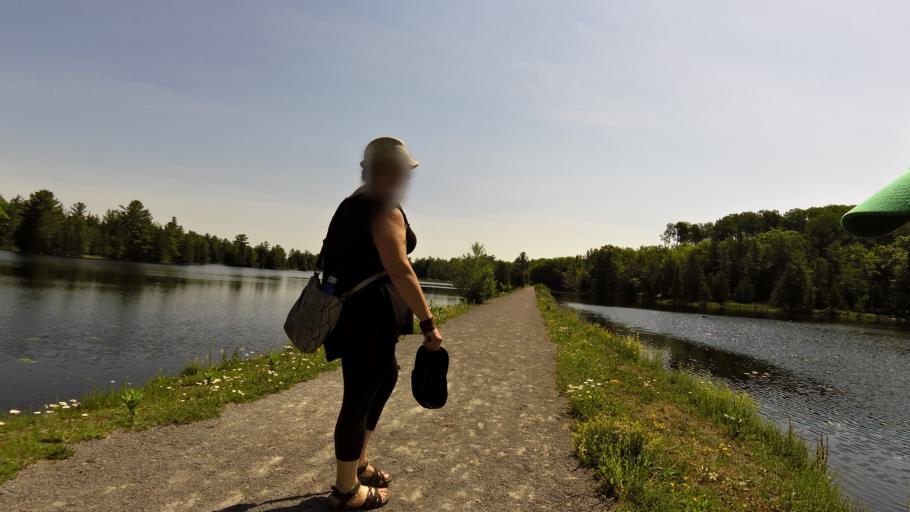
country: CA
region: Ontario
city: Arnprior
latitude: 45.4594
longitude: -76.2665
